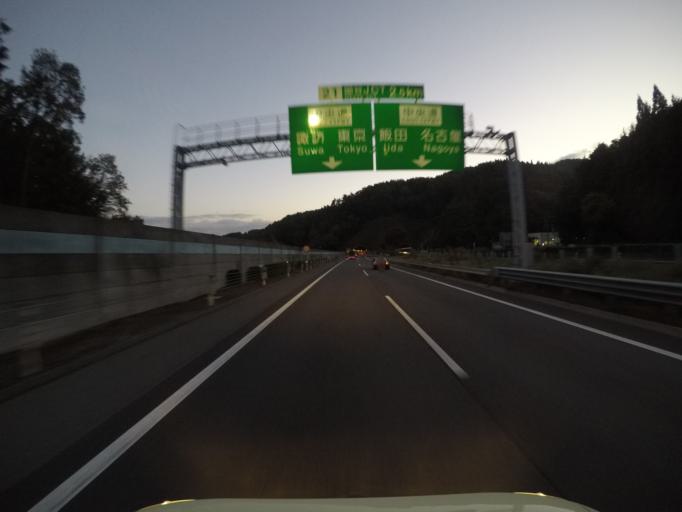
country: JP
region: Nagano
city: Okaya
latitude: 36.0740
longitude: 138.0384
